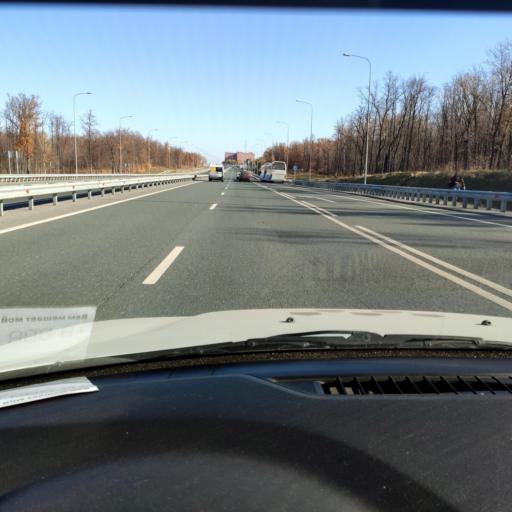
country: RU
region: Samara
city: Bereza
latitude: 53.5073
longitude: 50.1317
